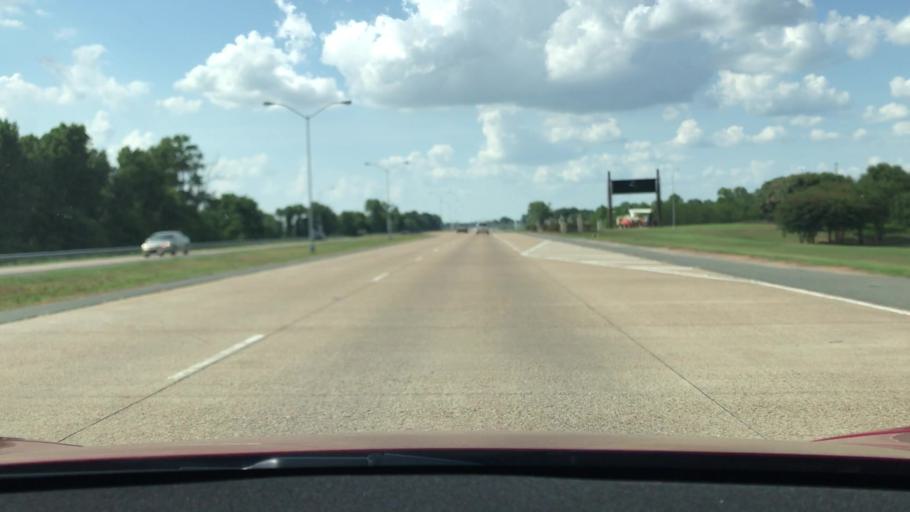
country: US
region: Louisiana
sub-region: Bossier Parish
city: Bossier City
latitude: 32.4630
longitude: -93.6761
